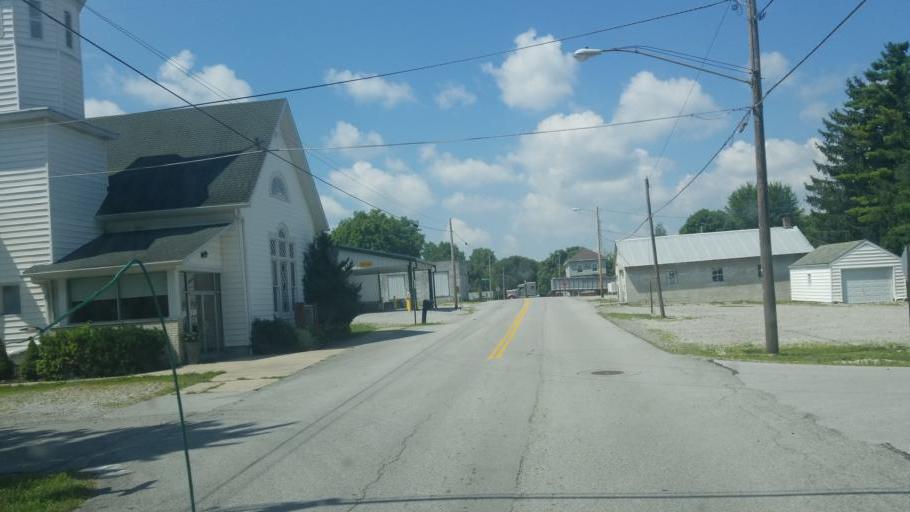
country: US
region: Ohio
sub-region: Allen County
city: Lima
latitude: 40.6939
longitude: -83.9787
